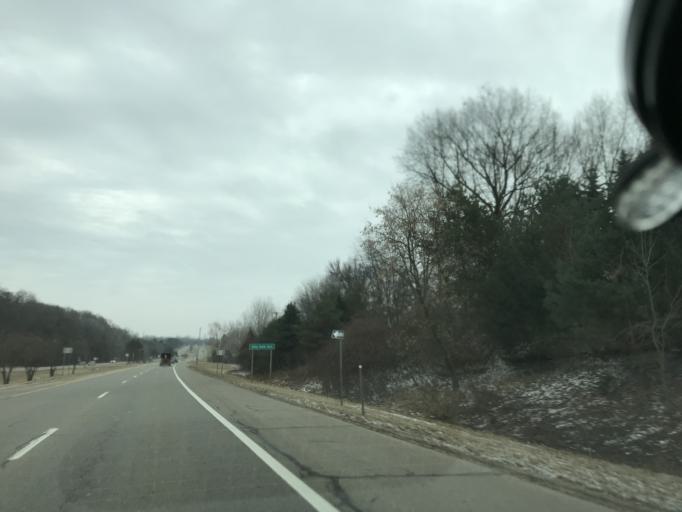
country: US
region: Michigan
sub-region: Kent County
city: Forest Hills
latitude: 42.9631
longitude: -85.5255
